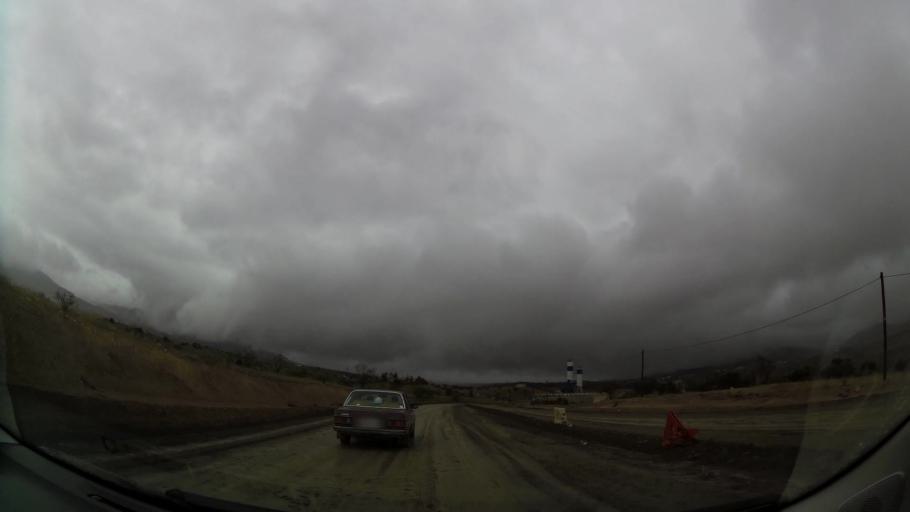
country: MA
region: Oriental
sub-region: Nador
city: Midar
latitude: 34.8957
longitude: -3.7705
